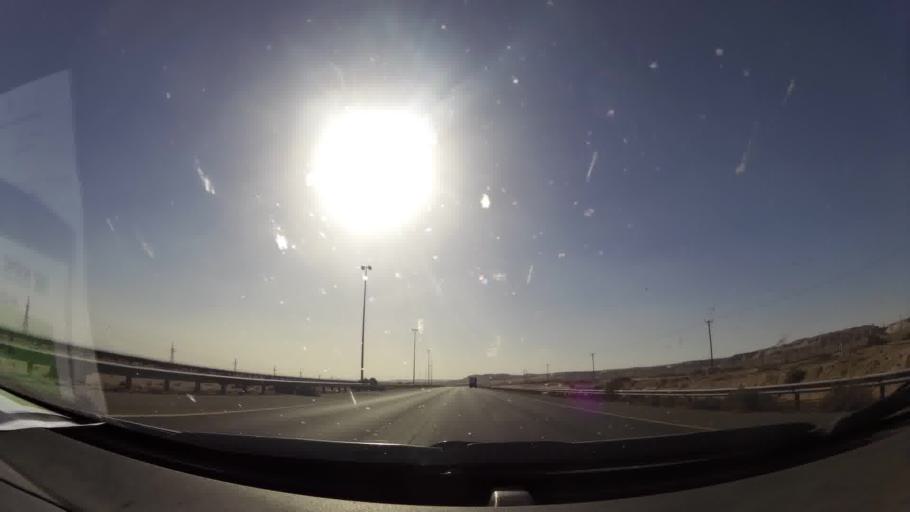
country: KW
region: Al Asimah
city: Kuwait City
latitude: 29.5192
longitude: 47.8099
